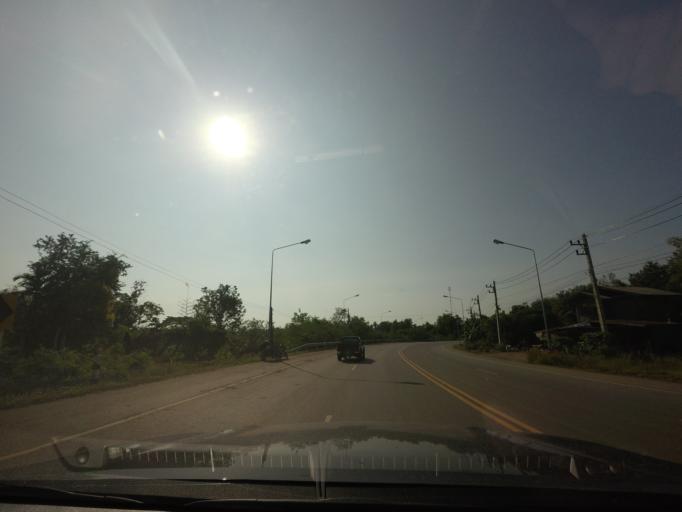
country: TH
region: Phetchabun
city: Lom Kao
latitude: 16.8383
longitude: 101.1814
